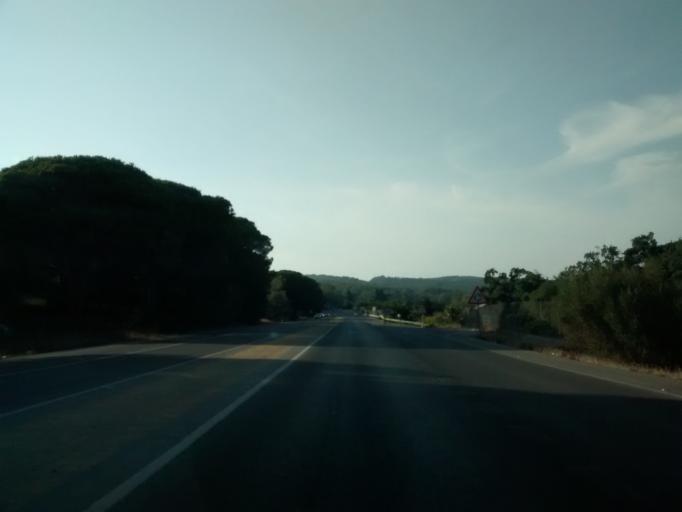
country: ES
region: Andalusia
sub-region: Provincia de Cadiz
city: Barbate de Franco
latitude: 36.2155
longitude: -5.9425
